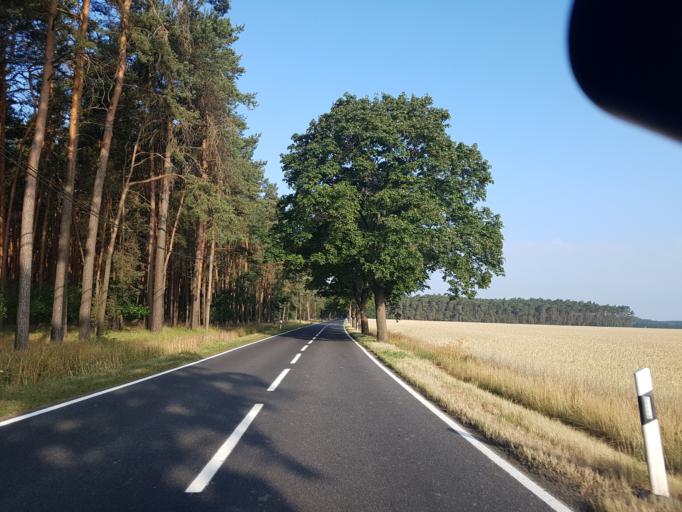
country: DE
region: Brandenburg
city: Ihlow
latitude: 51.8099
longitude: 13.2665
